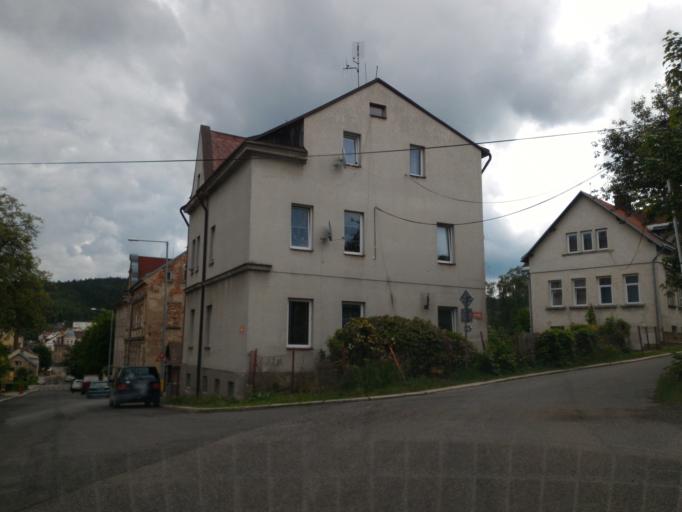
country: CZ
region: Liberecky
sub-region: Okres Jablonec nad Nisou
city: Jablonec nad Nisou
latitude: 50.7218
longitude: 15.1795
